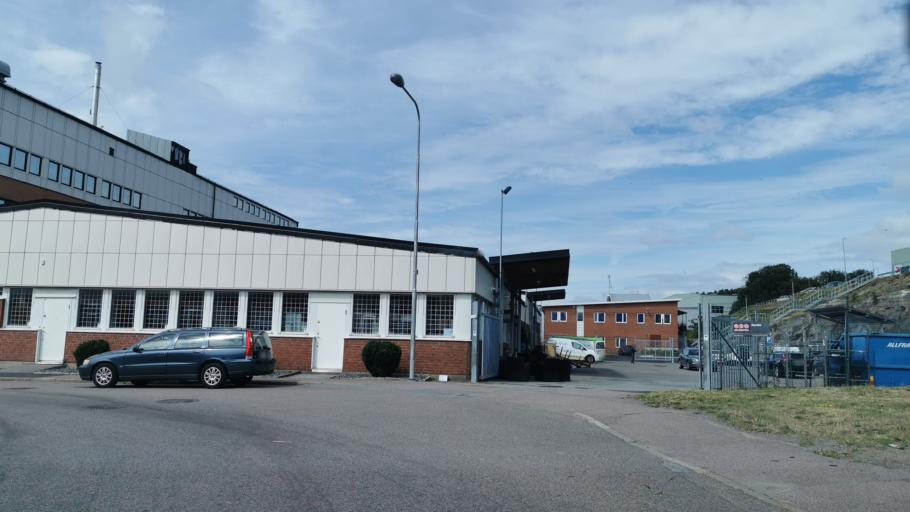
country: SE
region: Vaestra Goetaland
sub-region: Goteborg
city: Majorna
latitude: 57.6551
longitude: 11.9452
